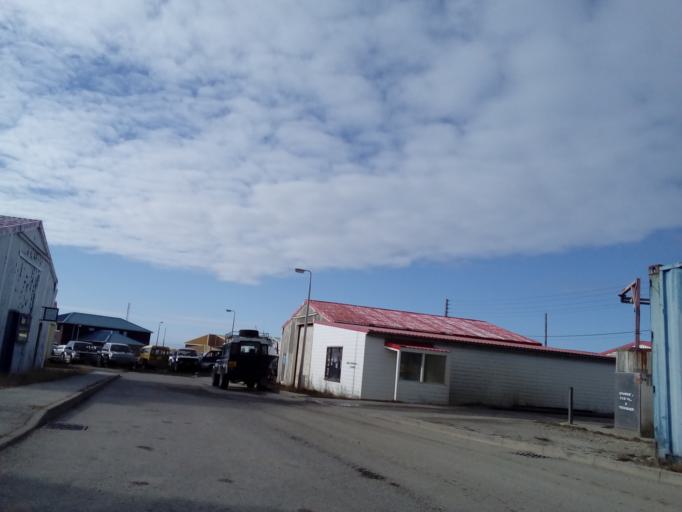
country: FK
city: Stanley
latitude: -51.6964
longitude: -57.8479
